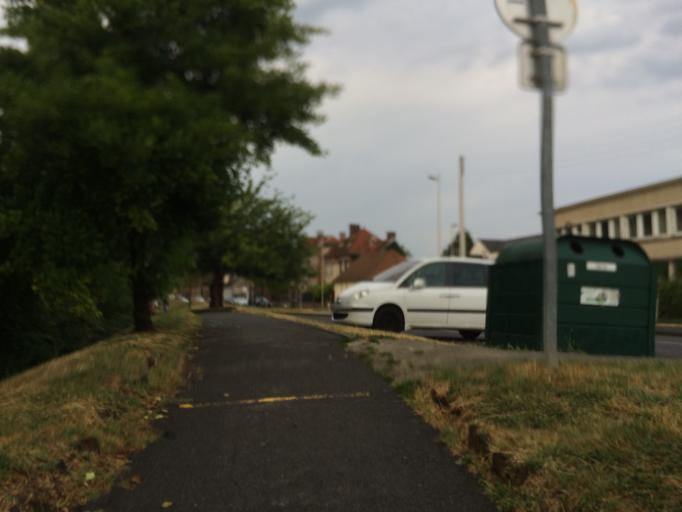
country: FR
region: Picardie
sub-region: Departement de l'Oise
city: Venette
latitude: 49.4138
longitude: 2.8116
